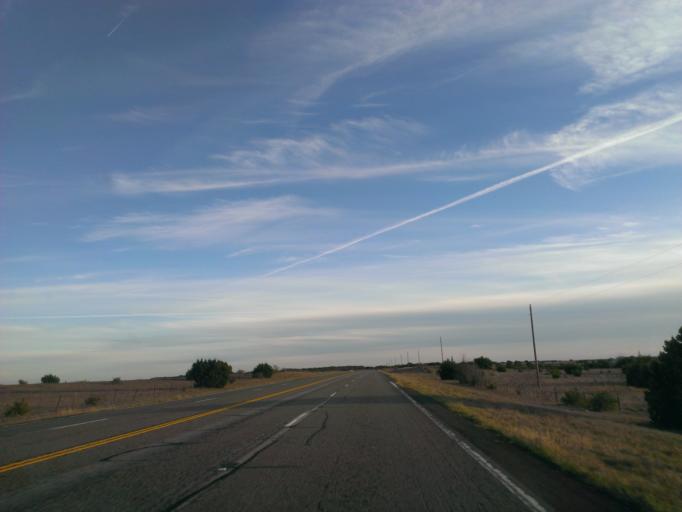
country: US
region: Texas
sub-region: Lampasas County
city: Kempner
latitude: 30.9078
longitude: -97.9725
